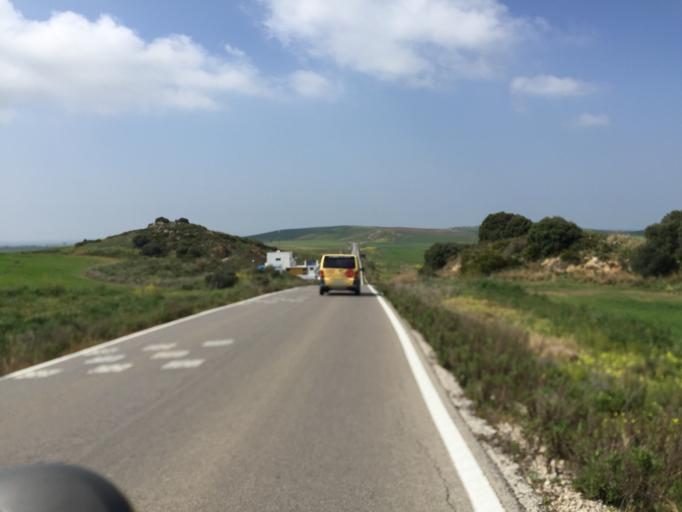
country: ES
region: Andalusia
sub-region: Provincia de Cadiz
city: Vejer de la Frontera
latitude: 36.2367
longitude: -6.0158
